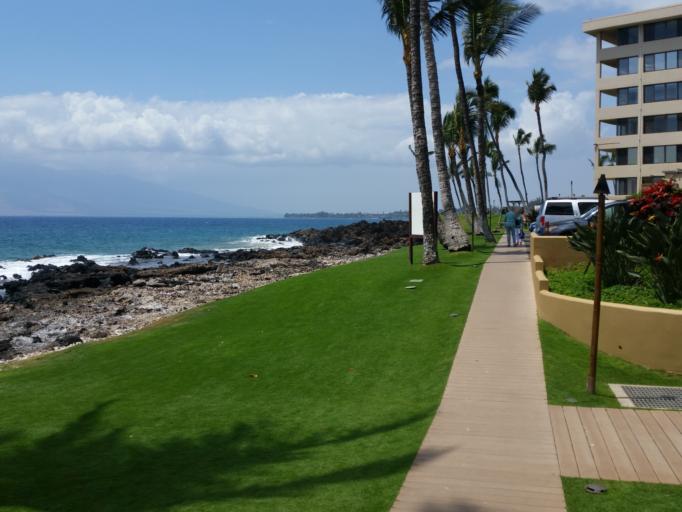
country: US
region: Hawaii
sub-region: Maui County
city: Kihei
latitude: 20.7050
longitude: -156.4469
